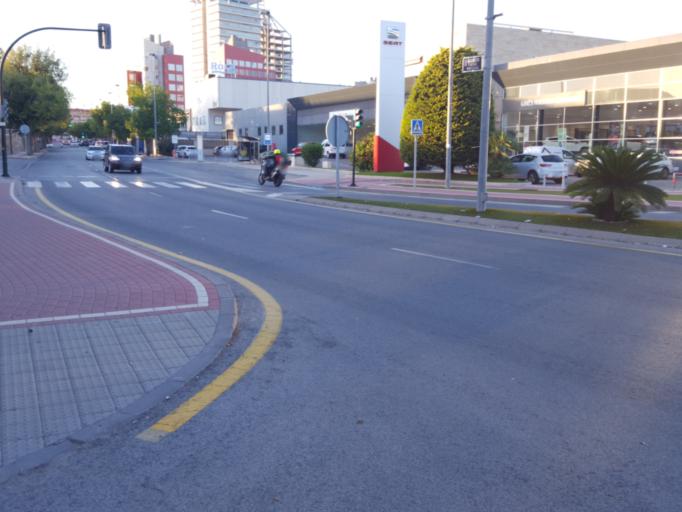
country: ES
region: Murcia
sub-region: Murcia
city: Murcia
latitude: 38.0035
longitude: -1.1471
